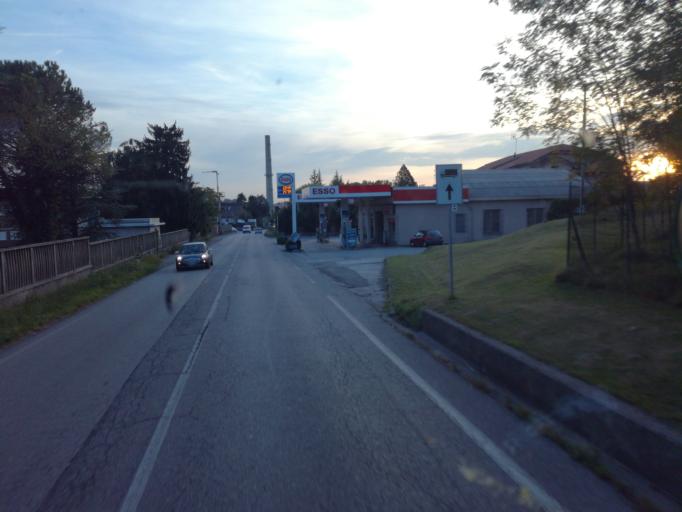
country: IT
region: Lombardy
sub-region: Provincia di Lecco
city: Bulciago
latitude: 45.7505
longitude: 9.2865
